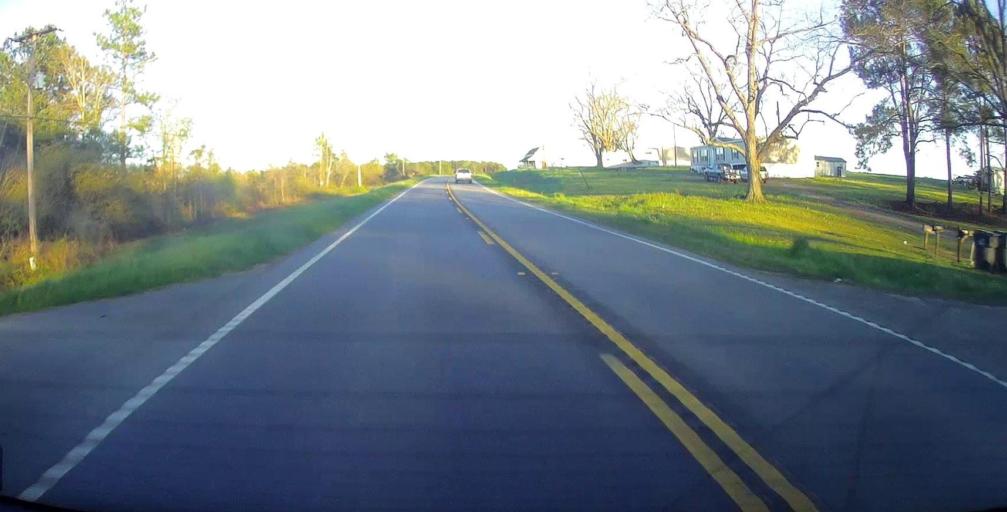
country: US
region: Georgia
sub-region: Crisp County
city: Cordele
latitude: 31.9560
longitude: -83.7296
